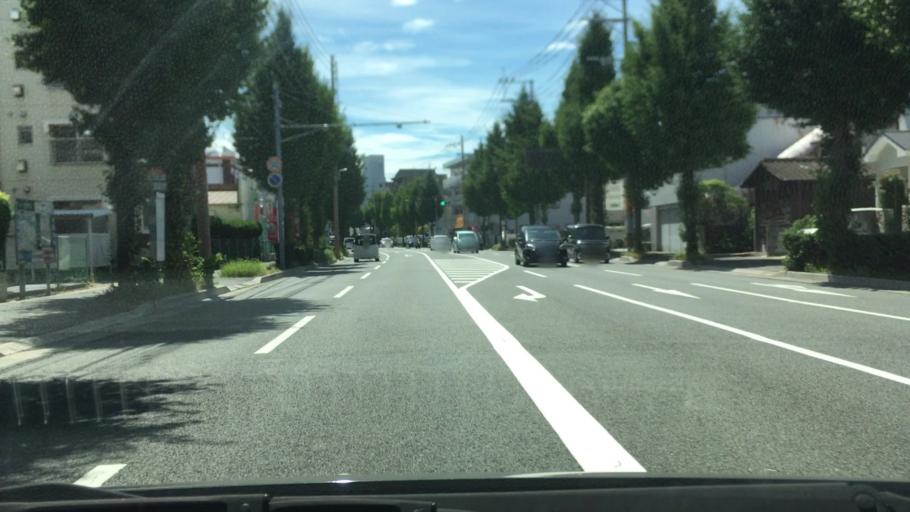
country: JP
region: Fukuoka
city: Fukuoka-shi
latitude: 33.5660
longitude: 130.4281
